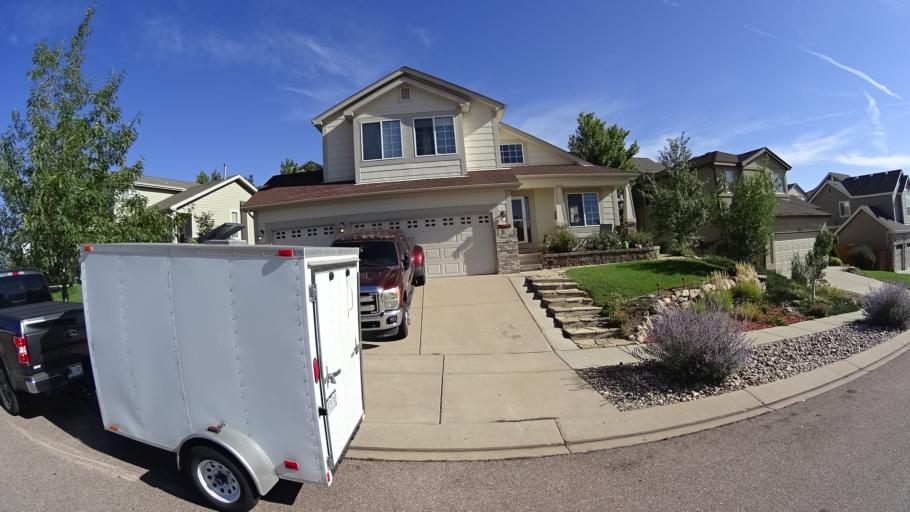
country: US
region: Colorado
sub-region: El Paso County
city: Black Forest
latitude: 38.9428
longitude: -104.7366
